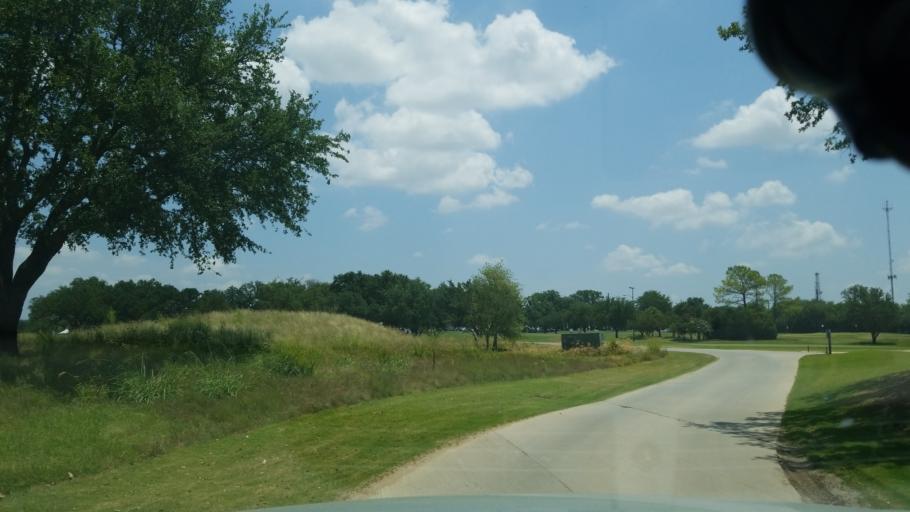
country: US
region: Texas
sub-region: Dallas County
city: Carrollton
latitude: 32.9632
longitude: -96.8726
